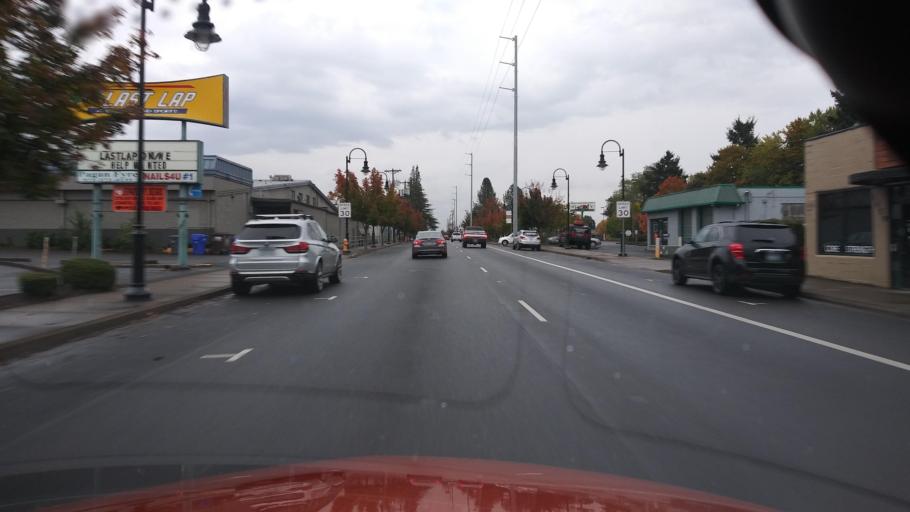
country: US
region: Oregon
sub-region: Washington County
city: Cornelius
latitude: 45.5201
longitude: -123.0542
